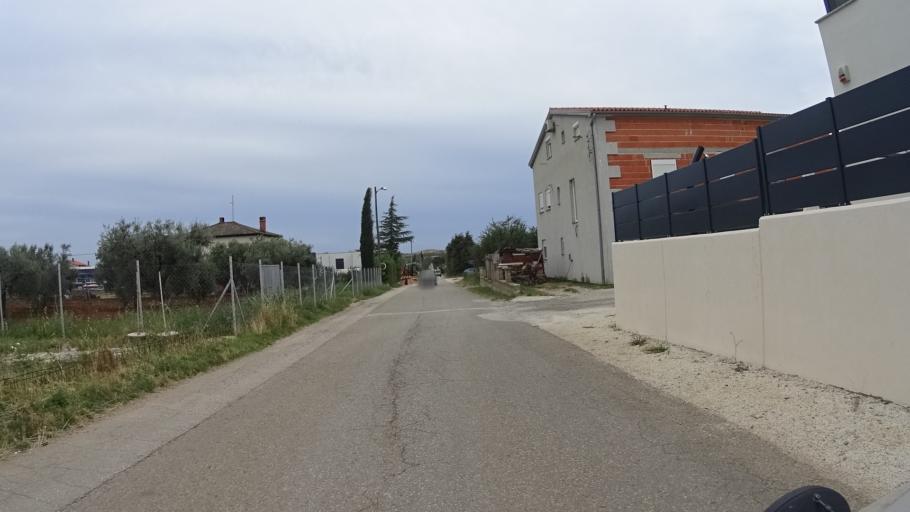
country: HR
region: Istarska
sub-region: Grad Pula
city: Pula
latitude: 44.8603
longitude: 13.8965
